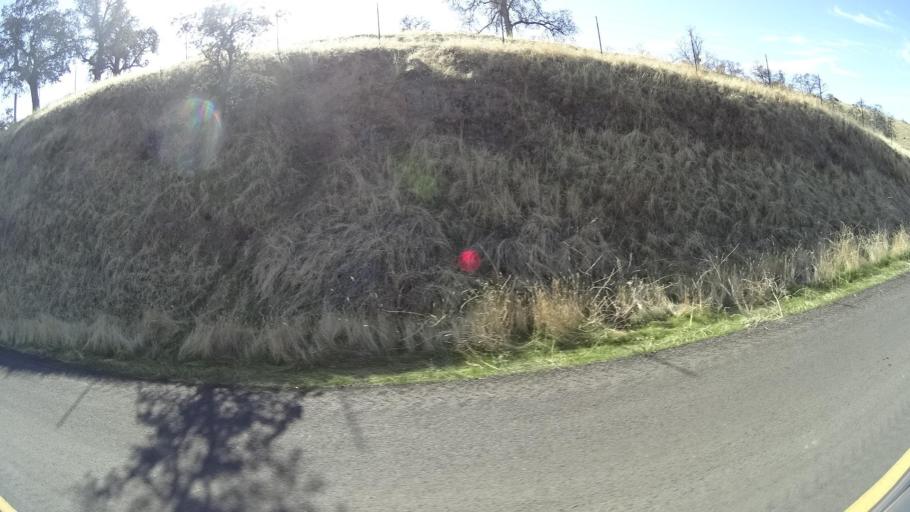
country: US
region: California
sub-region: Tulare County
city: Richgrove
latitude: 35.6982
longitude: -118.8407
